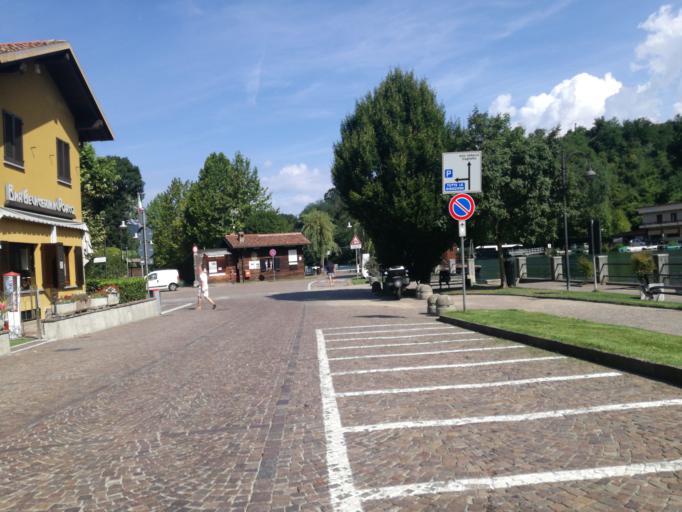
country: IT
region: Lombardy
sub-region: Provincia di Bergamo
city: Villa d'Adda
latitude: 45.7074
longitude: 9.4565
